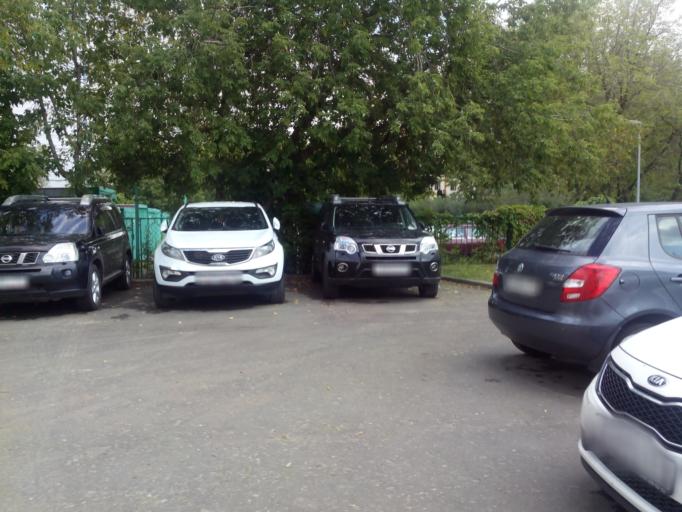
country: RU
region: Moscow
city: Ostankinskiy
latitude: 55.8253
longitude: 37.6252
